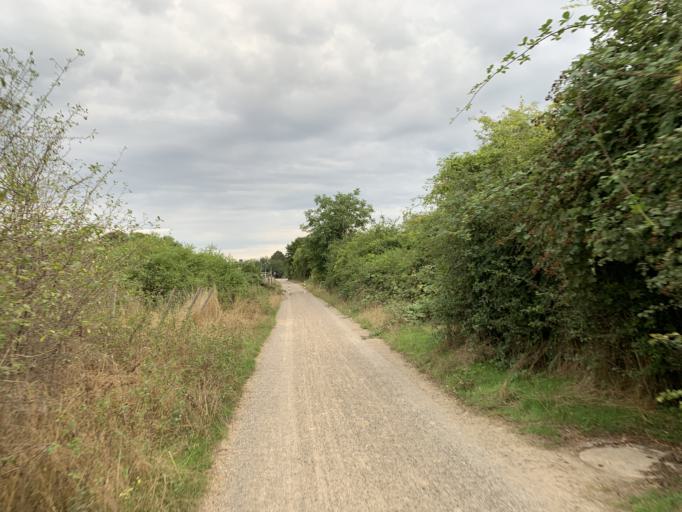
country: DE
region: North Rhine-Westphalia
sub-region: Regierungsbezirk Koln
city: Dueren
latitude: 50.7848
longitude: 6.4849
